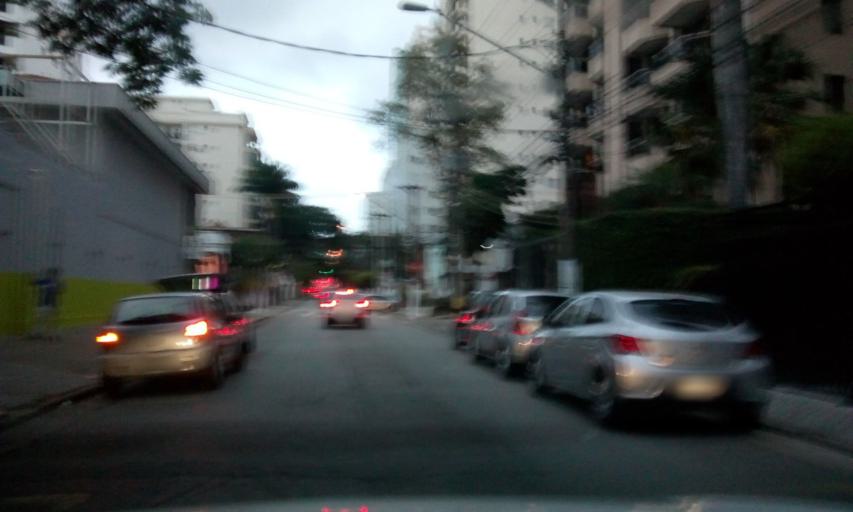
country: BR
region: Sao Paulo
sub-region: Sao Paulo
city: Sao Paulo
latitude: -23.6105
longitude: -46.6811
